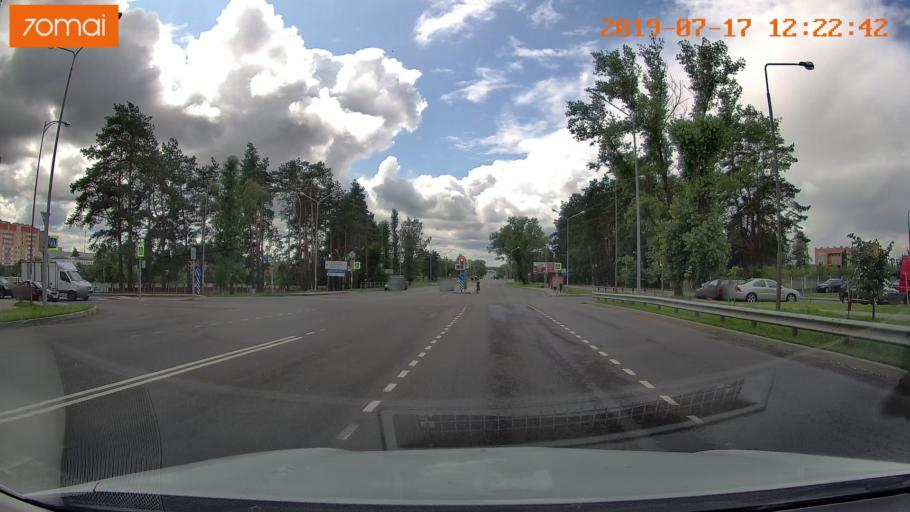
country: BY
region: Minsk
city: Borovlyany
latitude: 54.0001
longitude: 27.6766
